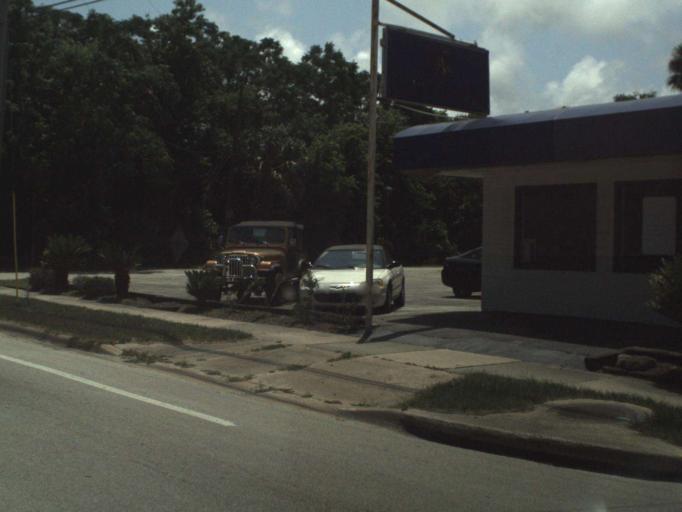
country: US
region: Florida
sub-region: Volusia County
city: Ormond Beach
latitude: 29.2806
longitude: -81.0608
